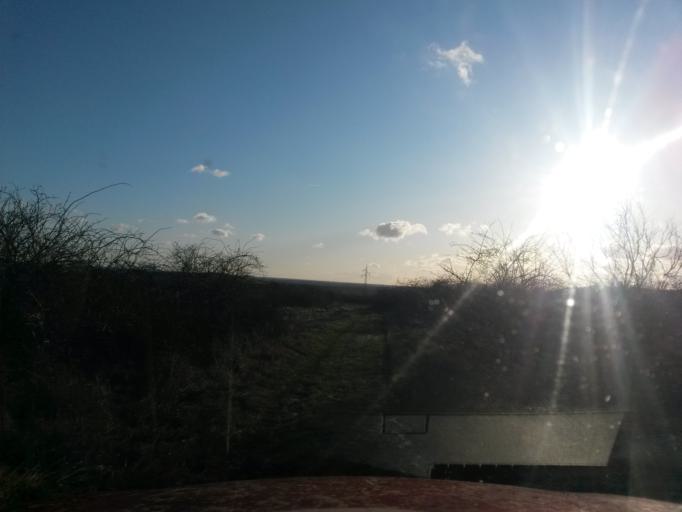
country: HU
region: Borsod-Abauj-Zemplen
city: Sarospatak
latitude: 48.3255
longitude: 21.5382
